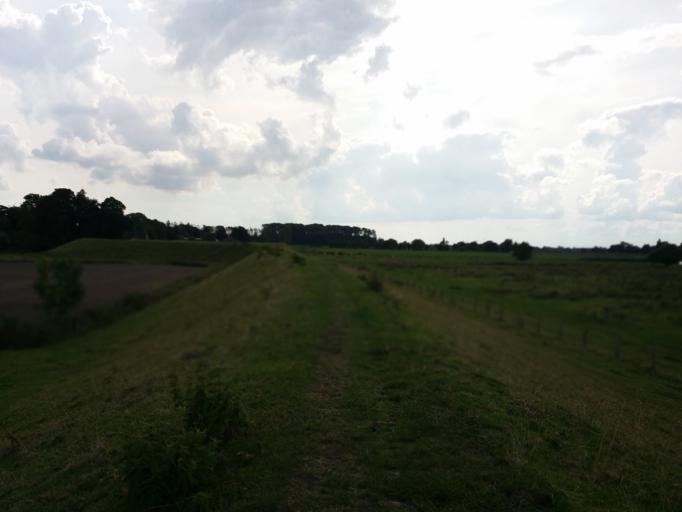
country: DE
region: Schleswig-Holstein
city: Bahrenfleth
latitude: 53.8690
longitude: 9.4273
